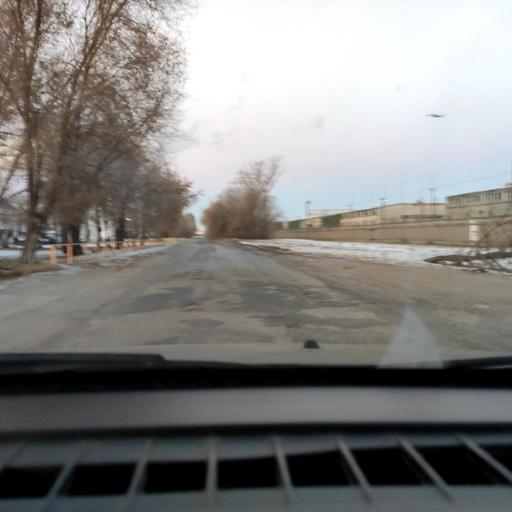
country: RU
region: Samara
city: Tol'yatti
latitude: 53.5783
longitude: 49.2742
